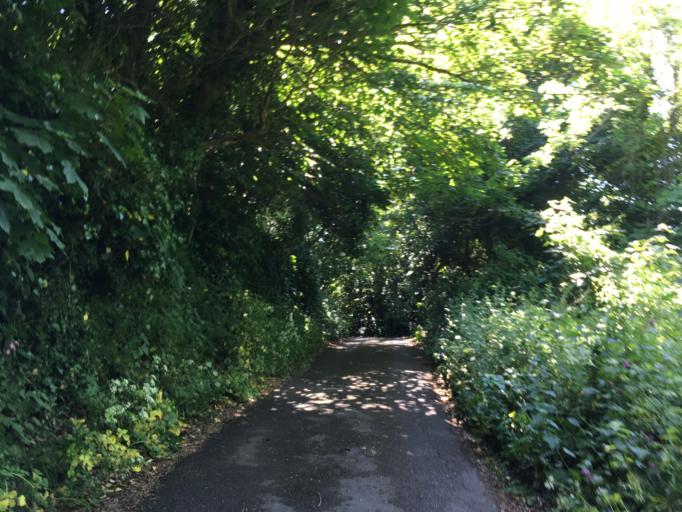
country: GB
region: England
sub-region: Devon
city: Dartmouth
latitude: 50.3449
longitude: -3.5628
